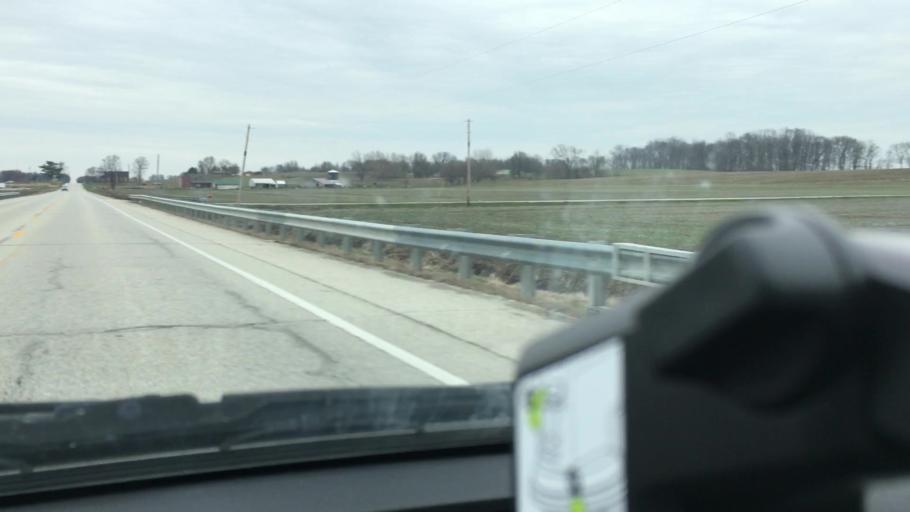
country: US
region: Indiana
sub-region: Greene County
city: Bloomfield
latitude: 38.9704
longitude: -87.0165
